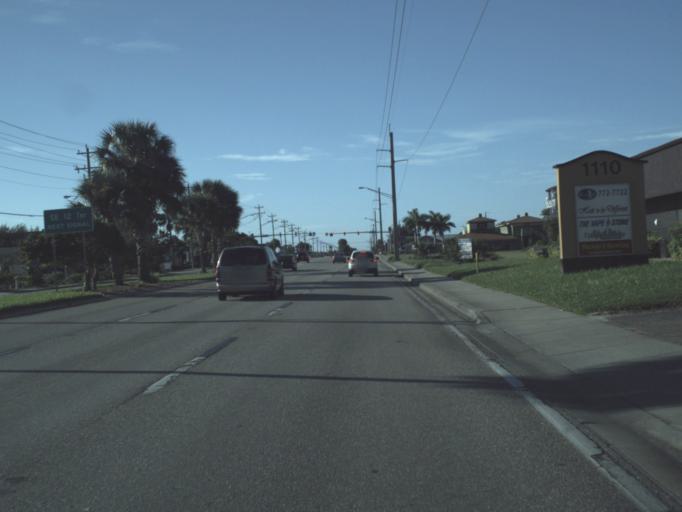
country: US
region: Florida
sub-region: Lee County
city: Lochmoor Waterway Estates
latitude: 26.6318
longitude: -81.9410
